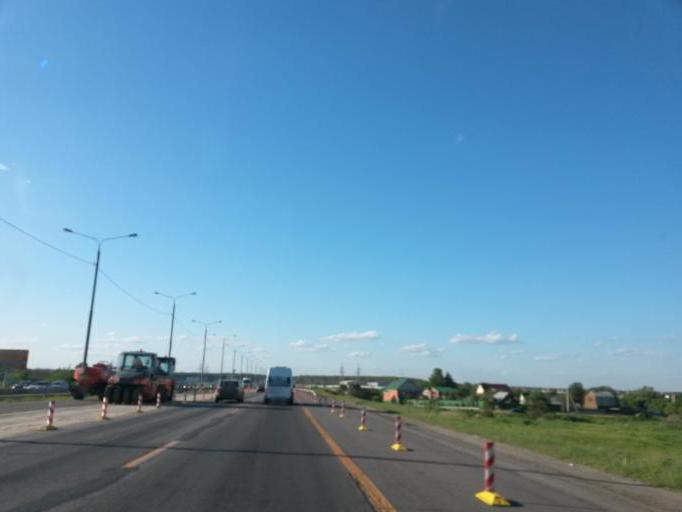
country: RU
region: Moskovskaya
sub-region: Podol'skiy Rayon
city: Podol'sk
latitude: 55.3796
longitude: 37.6051
